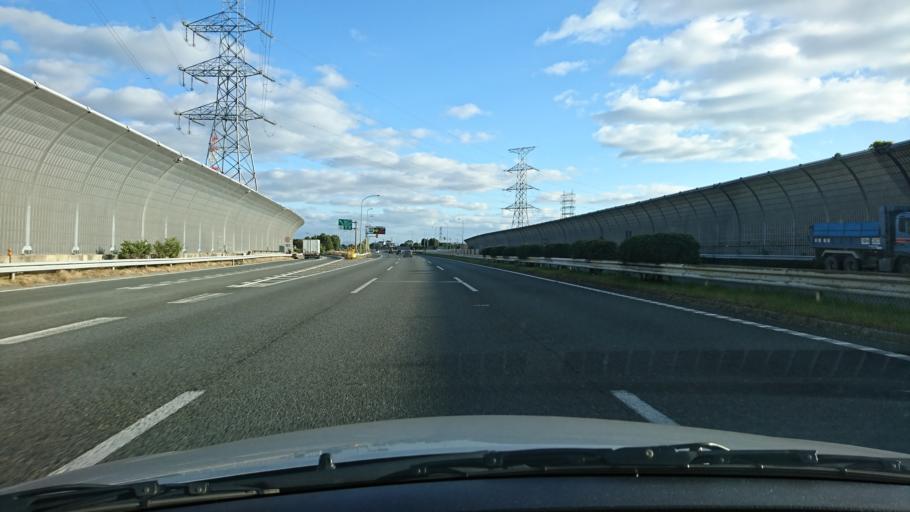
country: JP
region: Hyogo
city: Takarazuka
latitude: 34.8084
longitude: 135.3660
